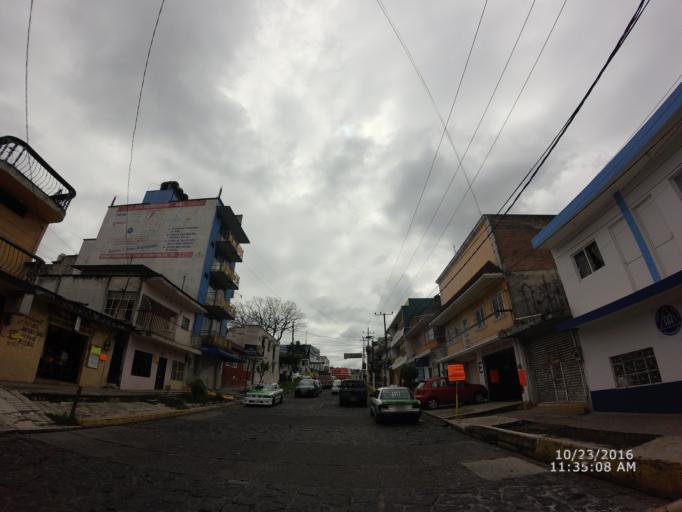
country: MX
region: Veracruz
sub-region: Xalapa
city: Xalapa de Enriquez
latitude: 19.5372
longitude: -96.9310
